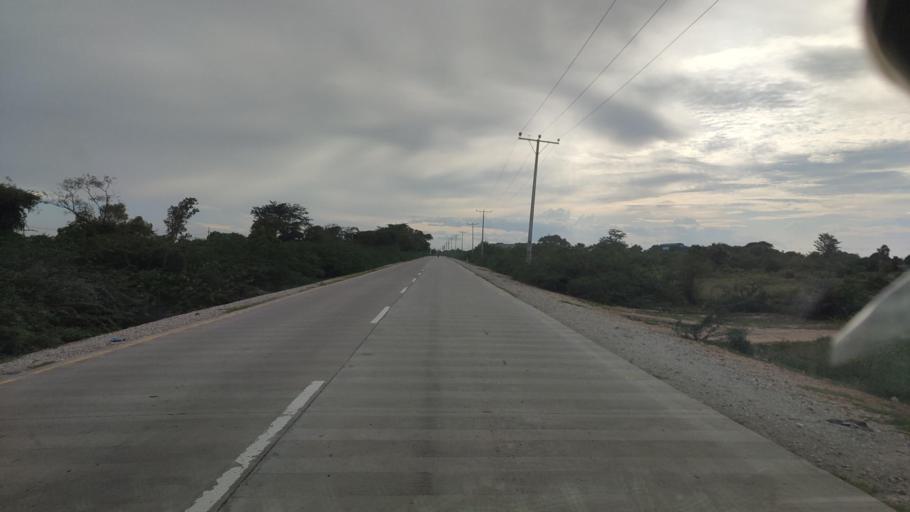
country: MM
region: Mandalay
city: Kyaukse
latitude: 21.3454
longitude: 96.0917
